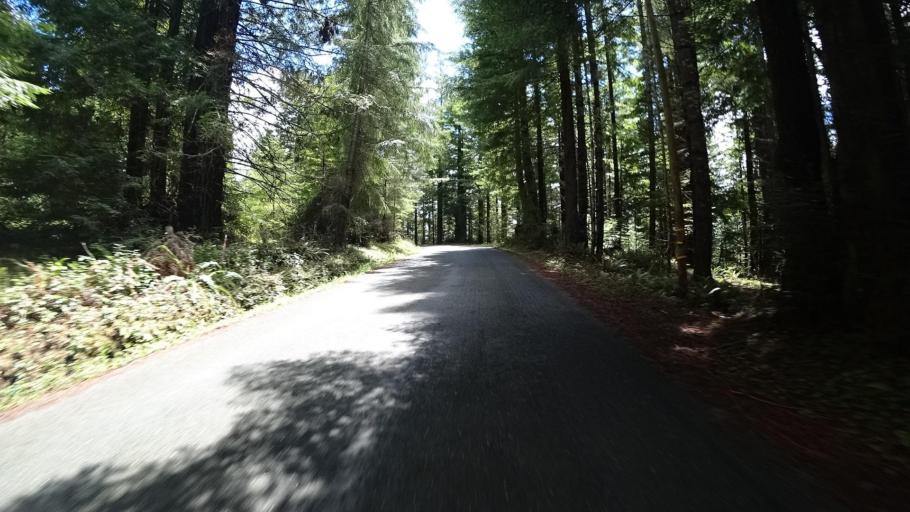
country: US
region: California
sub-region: Humboldt County
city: Blue Lake
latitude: 40.8456
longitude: -123.9242
